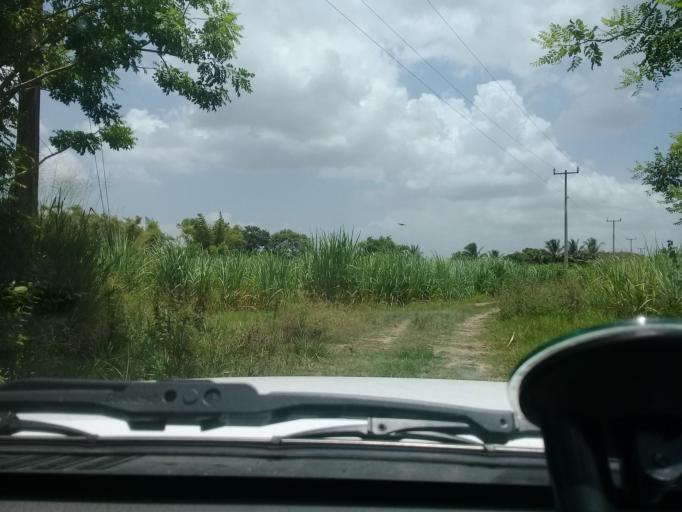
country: MX
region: Veracruz
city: Moralillo
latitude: 22.1358
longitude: -98.0404
